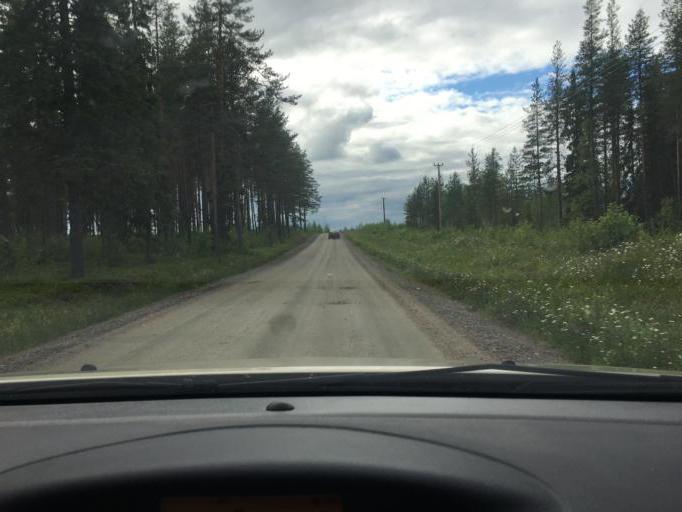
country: SE
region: Norrbotten
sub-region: Overkalix Kommun
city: OEverkalix
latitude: 66.0895
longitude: 22.8376
